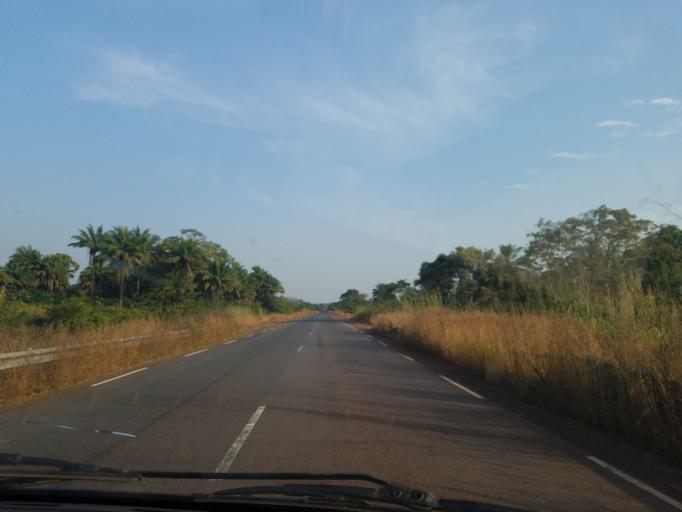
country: GN
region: Boke
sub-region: Boffa
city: Boffa
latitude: 10.3469
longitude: -14.2455
